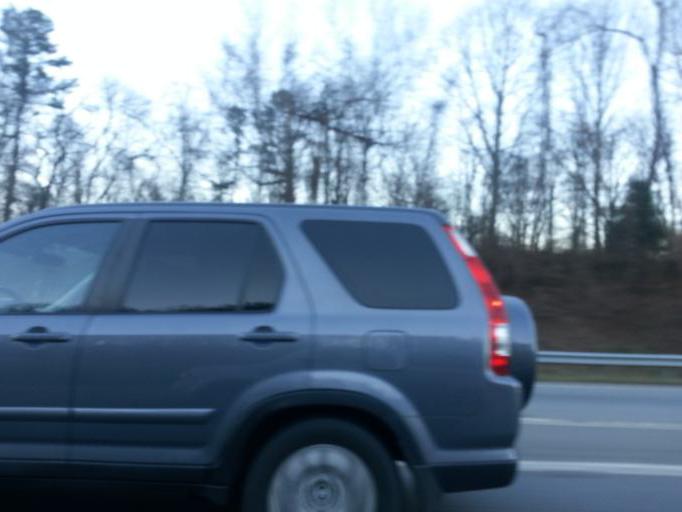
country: US
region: North Carolina
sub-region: Buncombe County
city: Bent Creek
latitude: 35.5484
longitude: -82.6067
